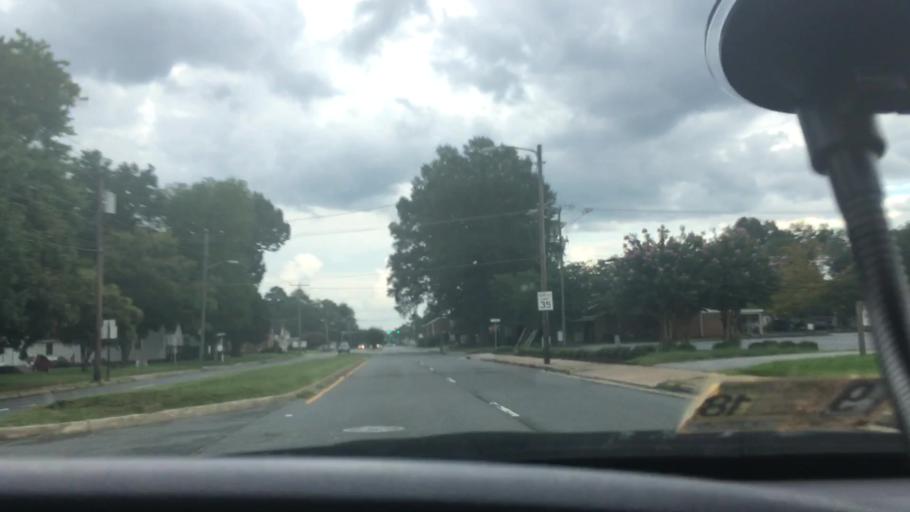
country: US
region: Virginia
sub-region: City of Portsmouth
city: Portsmouth Heights
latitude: 36.8190
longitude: -76.3769
